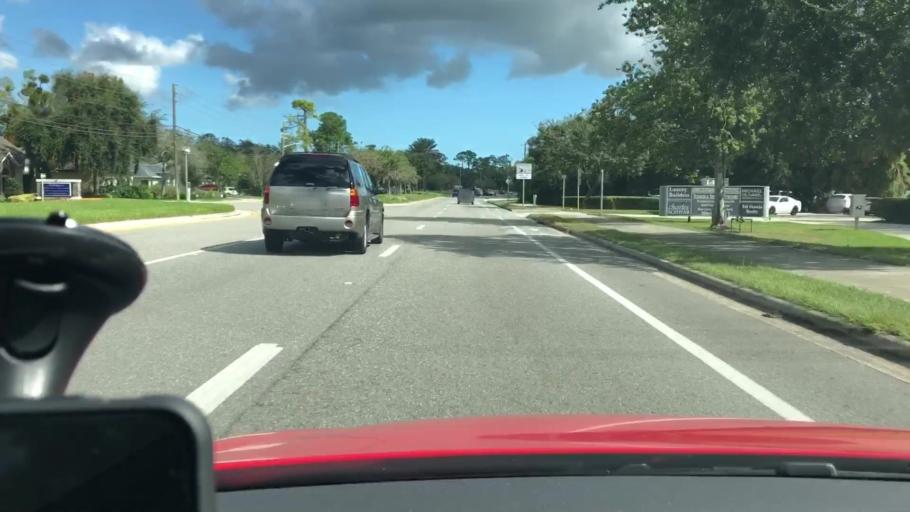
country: US
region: Florida
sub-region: Volusia County
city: Ormond Beach
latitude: 29.2604
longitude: -81.1093
